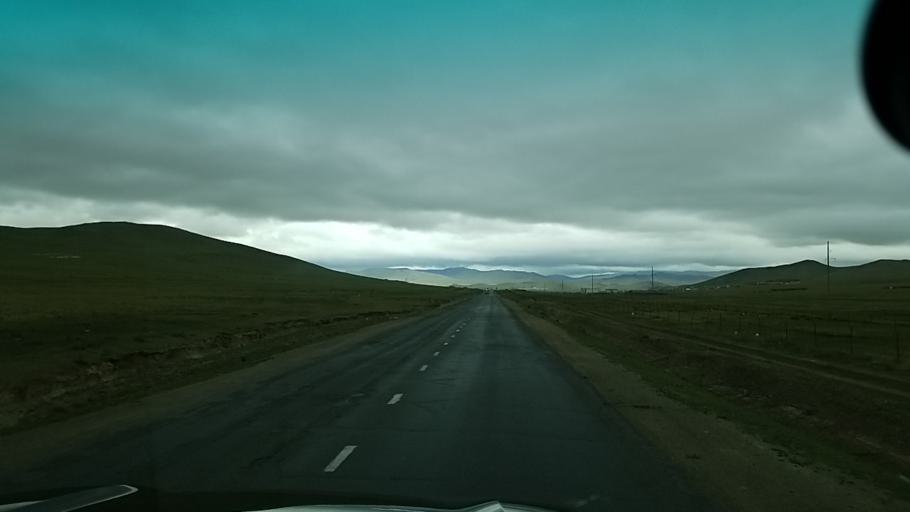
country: MN
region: Ulaanbaatar
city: Ulaanbaatar
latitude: 47.9817
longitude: 106.5696
